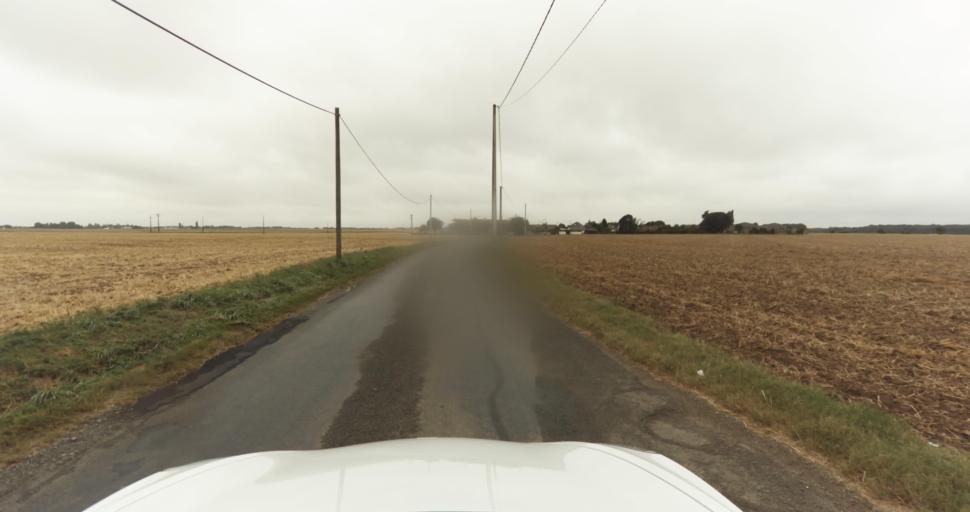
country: FR
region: Haute-Normandie
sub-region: Departement de l'Eure
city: Aviron
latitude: 49.0716
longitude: 1.0952
